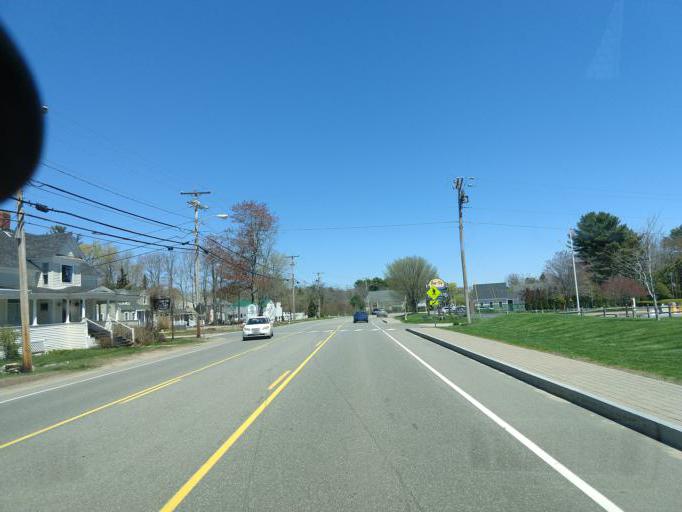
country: US
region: Maine
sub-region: York County
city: Wells Beach Station
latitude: 43.3267
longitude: -70.5774
